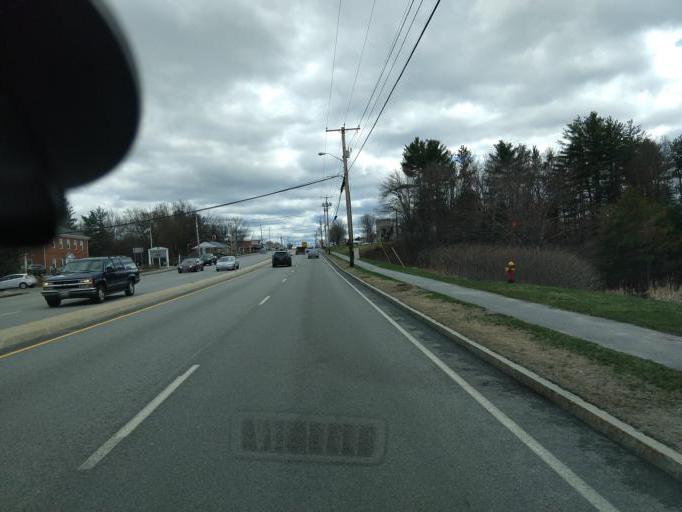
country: US
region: New Hampshire
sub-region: Rockingham County
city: Plaistow
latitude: 42.8214
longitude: -71.1043
